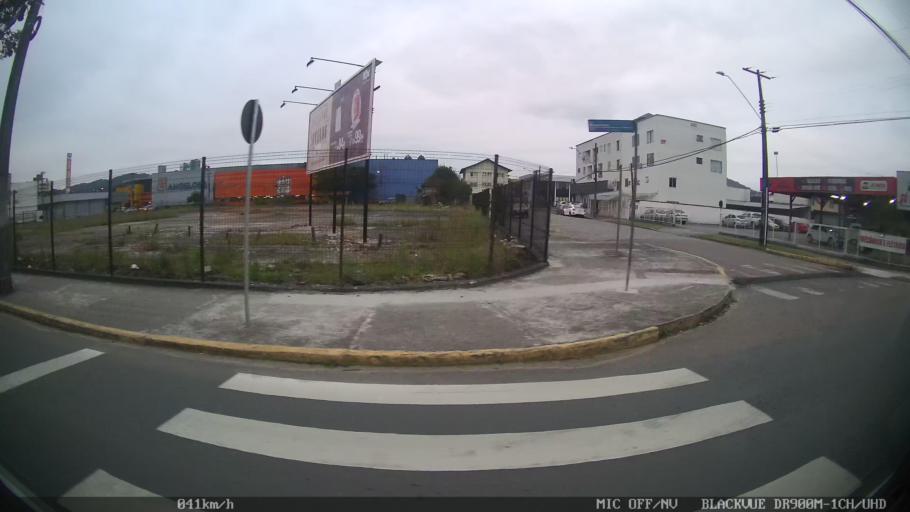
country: BR
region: Santa Catarina
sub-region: Joinville
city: Joinville
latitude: -26.2792
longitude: -48.8505
